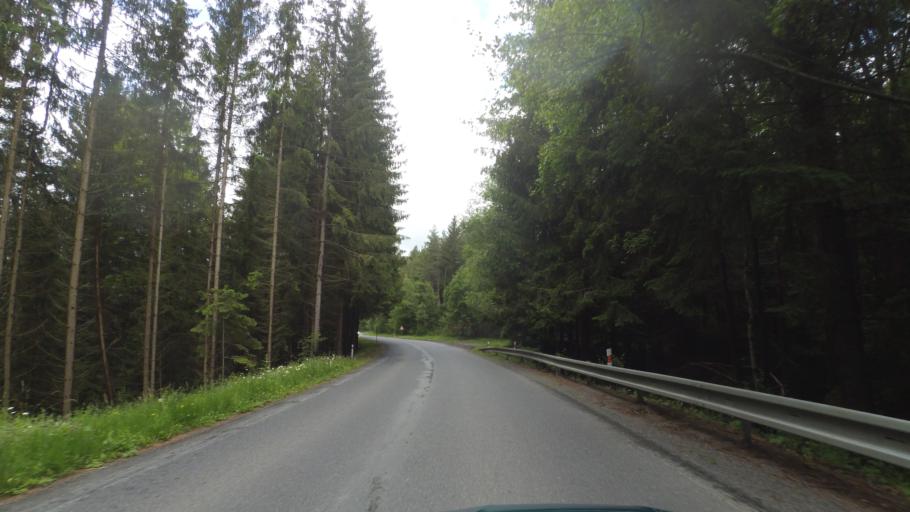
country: CZ
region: Plzensky
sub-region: Okres Klatovy
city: Nyrsko
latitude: 49.2588
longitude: 13.1576
